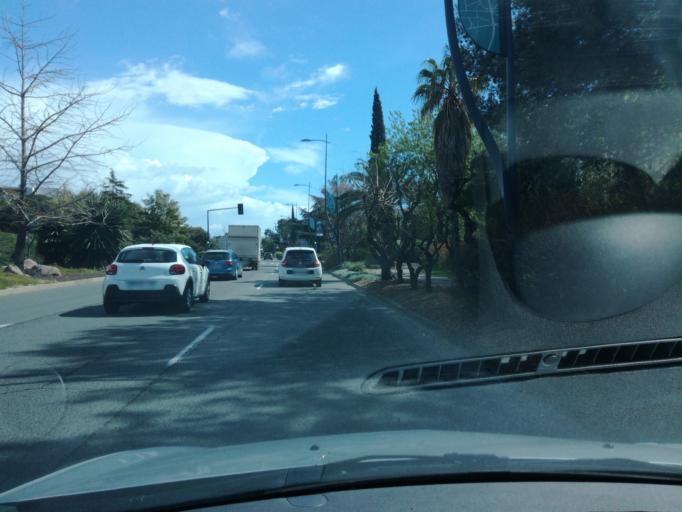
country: FR
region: Provence-Alpes-Cote d'Azur
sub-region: Departement du Var
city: Hyeres
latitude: 43.1135
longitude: 6.1310
